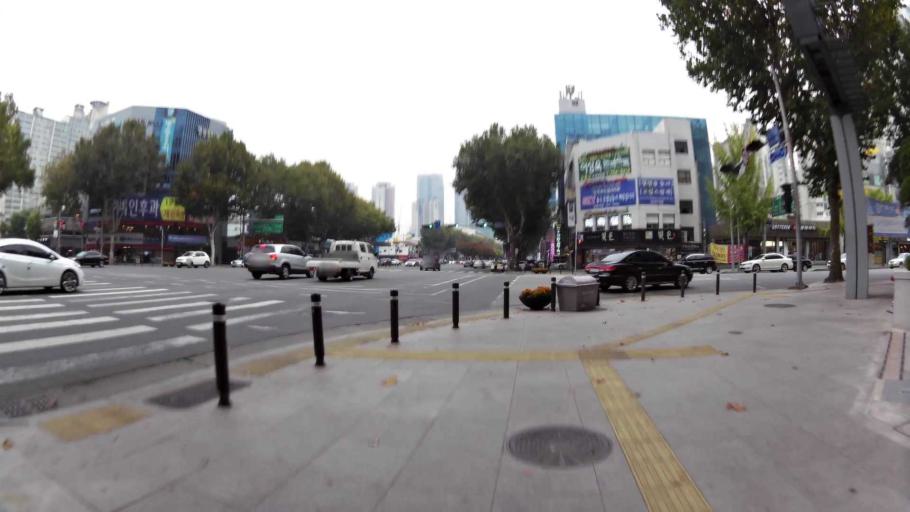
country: KR
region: Daegu
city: Daegu
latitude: 35.8594
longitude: 128.6173
